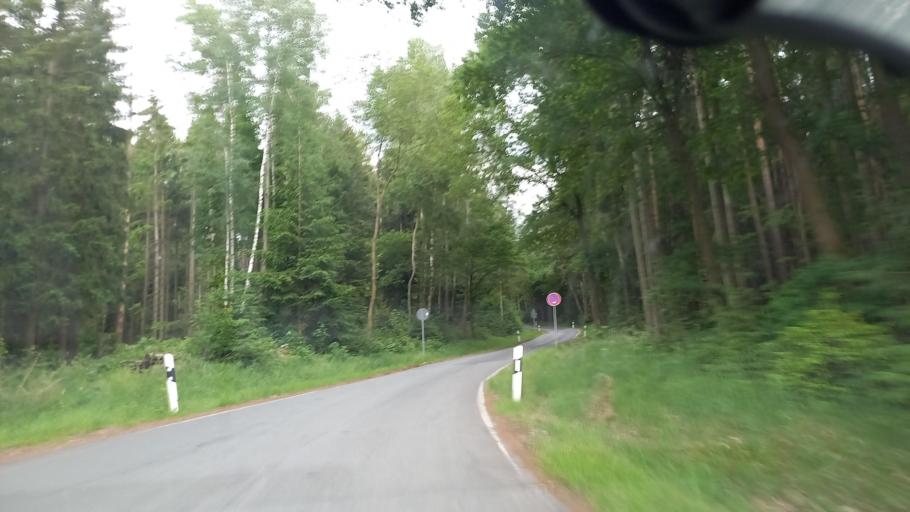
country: DE
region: Saxony
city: Waldkirchen
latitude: 50.6243
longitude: 12.4014
